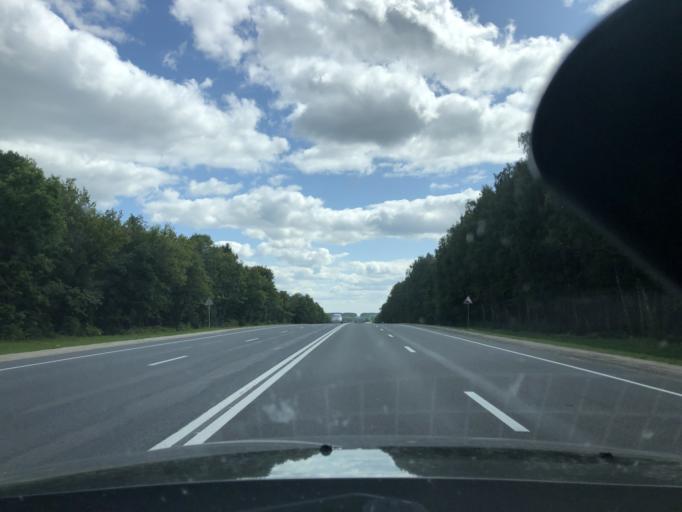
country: RU
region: Tula
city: Gorelki
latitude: 54.3149
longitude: 37.5642
